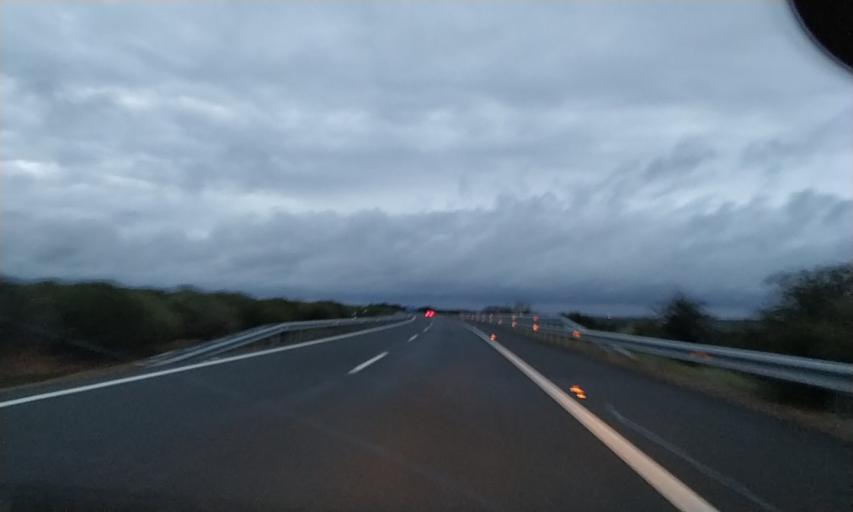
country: ES
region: Extremadura
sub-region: Provincia de Caceres
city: Casas de Don Antonio
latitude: 39.2157
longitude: -6.2892
